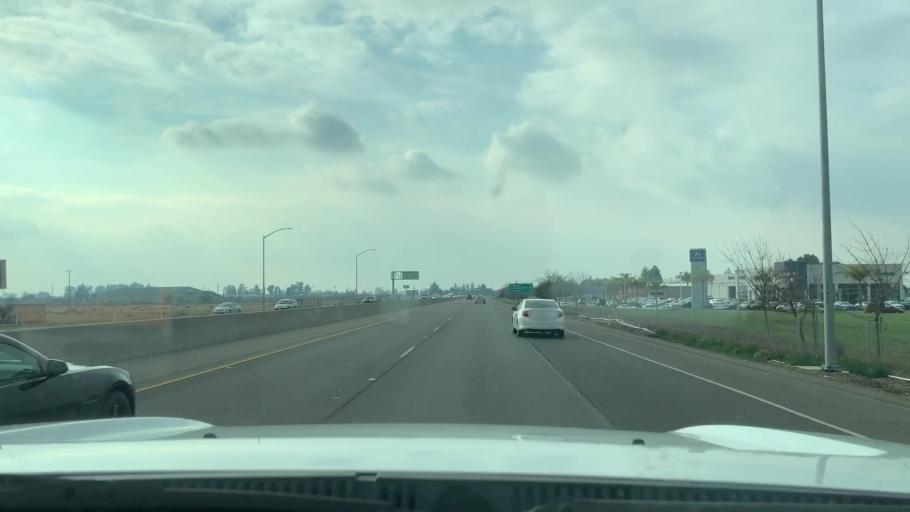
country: US
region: California
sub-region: Kings County
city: Armona
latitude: 36.3181
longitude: -119.6769
